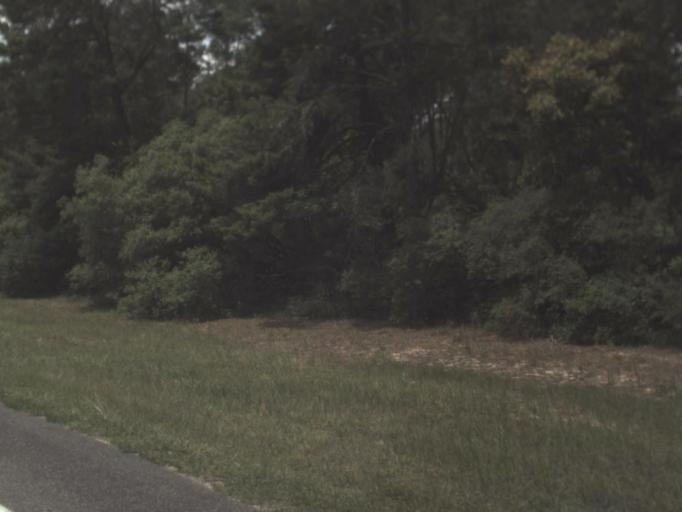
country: US
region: Florida
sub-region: Putnam County
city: Crescent City
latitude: 29.3821
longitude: -81.7361
